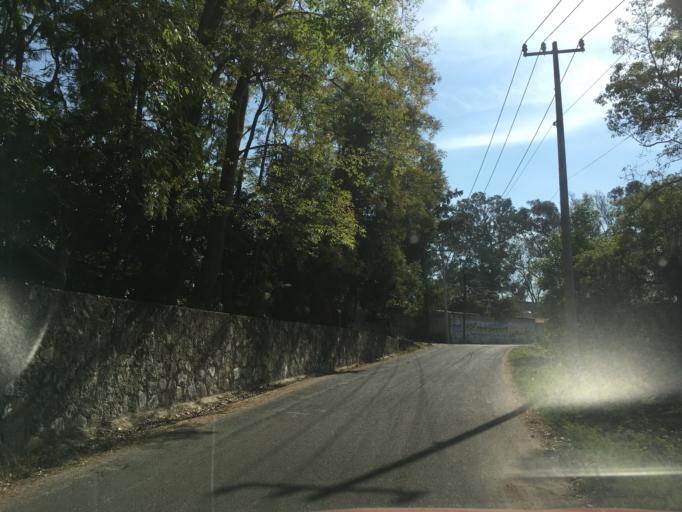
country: MX
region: Michoacan
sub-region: Zitacuaro
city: Valle Verde
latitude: 19.4697
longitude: -100.3436
